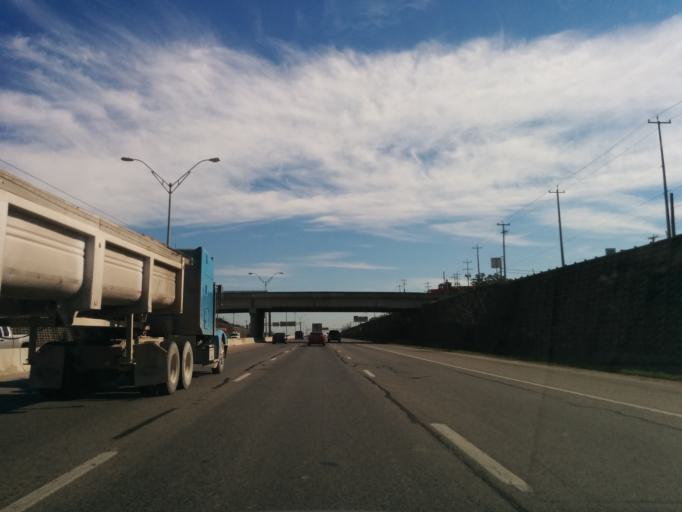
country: US
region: Texas
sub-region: Bexar County
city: Shavano Park
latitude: 29.5920
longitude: -98.5877
